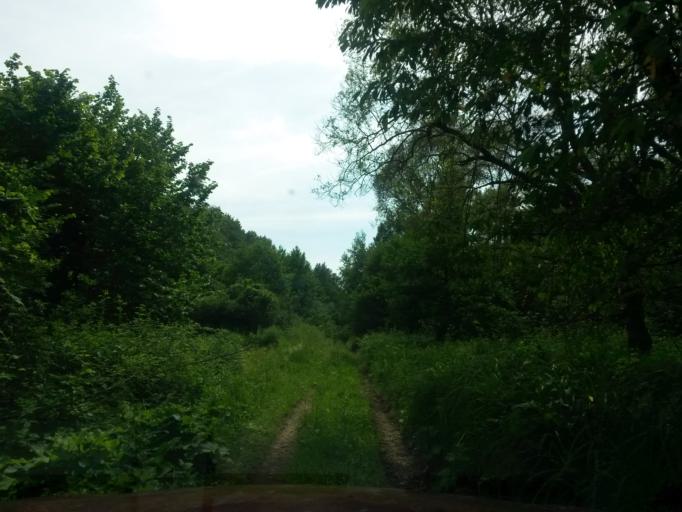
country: SK
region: Kosicky
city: Moldava nad Bodvou
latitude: 48.6495
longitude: 21.1064
